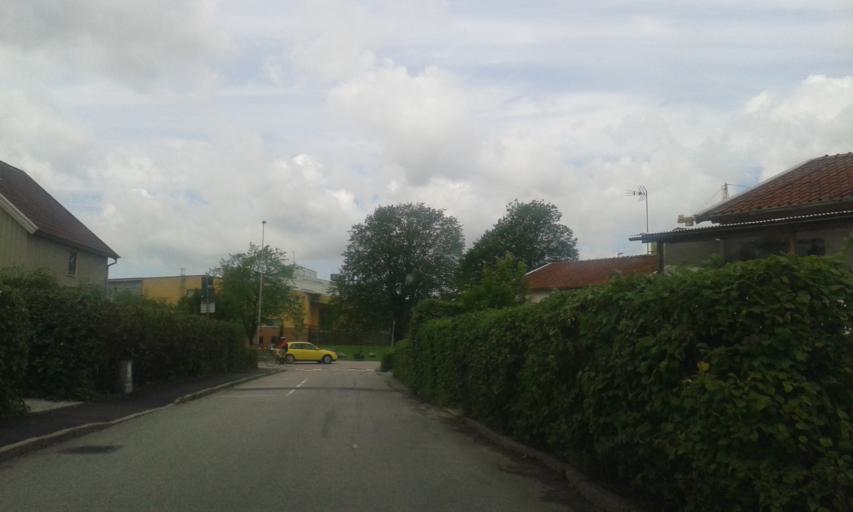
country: SE
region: Vaestra Goetaland
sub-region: Kungalvs Kommun
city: Kungalv
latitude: 57.8725
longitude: 11.9756
